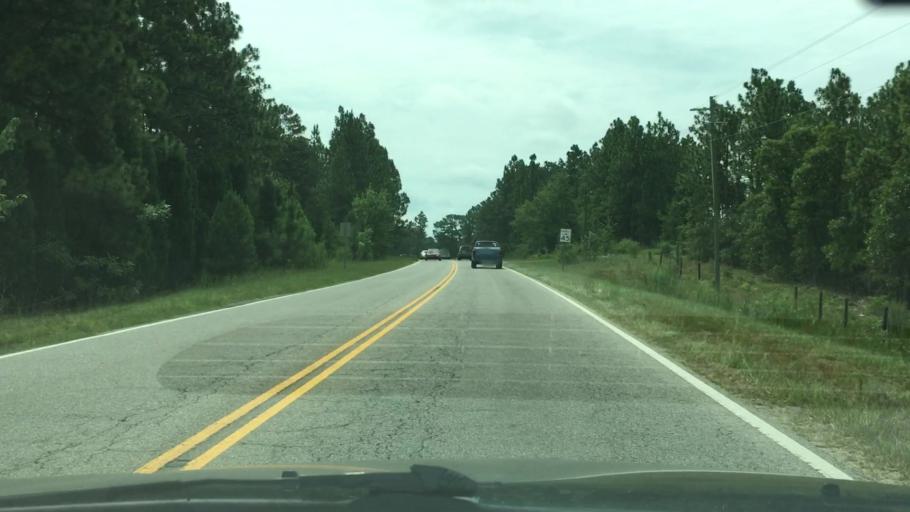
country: US
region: South Carolina
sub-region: Aiken County
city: Warrenville
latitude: 33.5318
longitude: -81.7704
